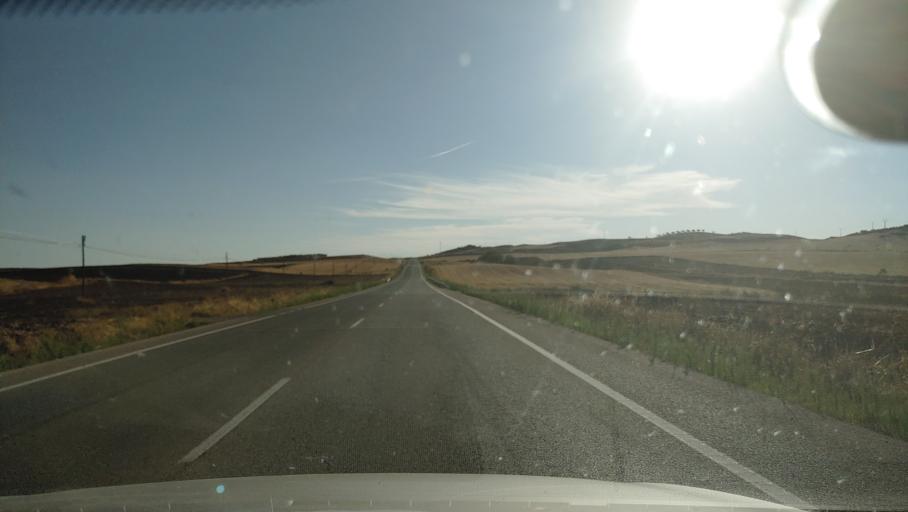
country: ES
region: Castille-La Mancha
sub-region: Provincia de Ciudad Real
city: Fuenllana
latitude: 38.7509
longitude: -2.9663
